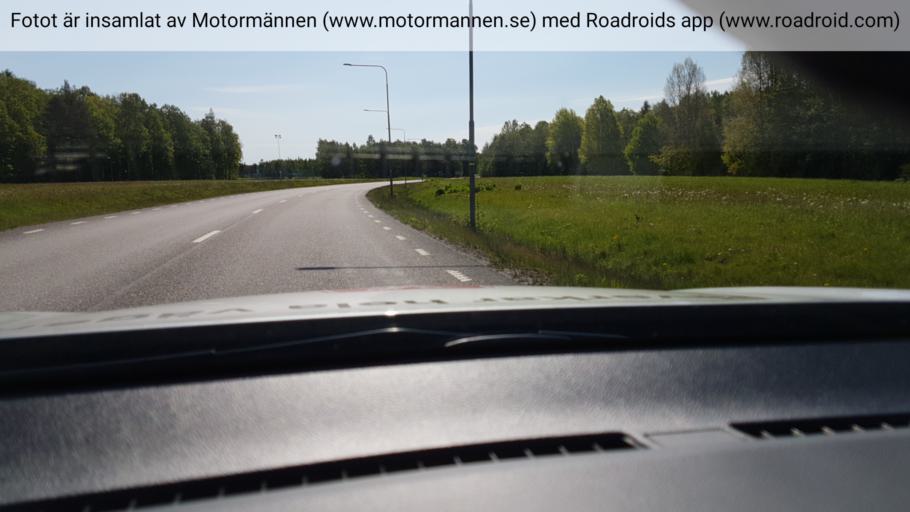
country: SE
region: Vaestra Goetaland
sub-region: Tibro Kommun
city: Tibro
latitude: 58.4135
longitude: 14.1624
